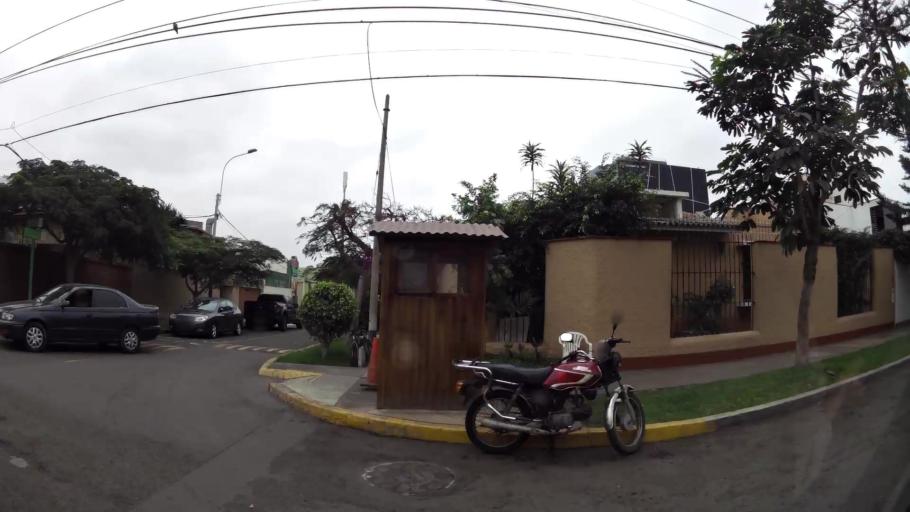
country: PE
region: Lima
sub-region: Lima
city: Surco
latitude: -12.1265
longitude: -77.0115
